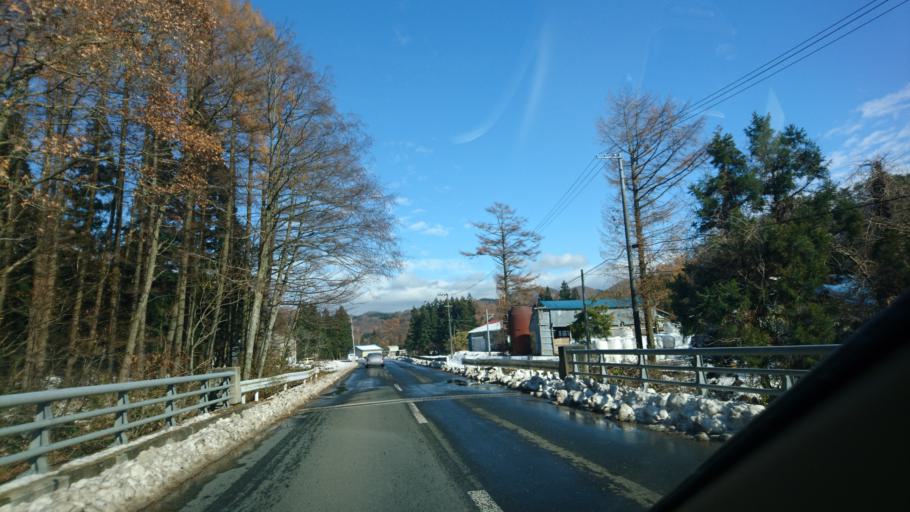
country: JP
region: Akita
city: Yokotemachi
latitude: 39.3417
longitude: 140.7605
